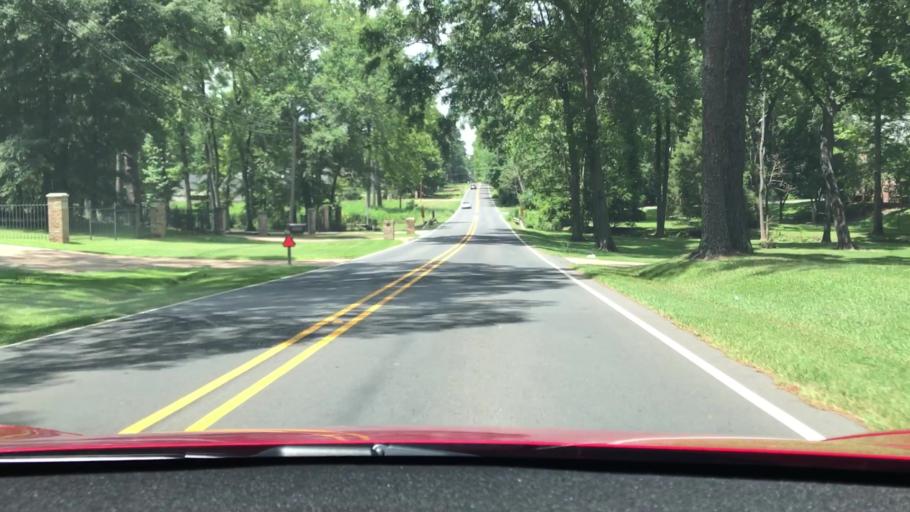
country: US
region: Louisiana
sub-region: Bossier Parish
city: Bossier City
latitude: 32.3765
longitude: -93.7137
